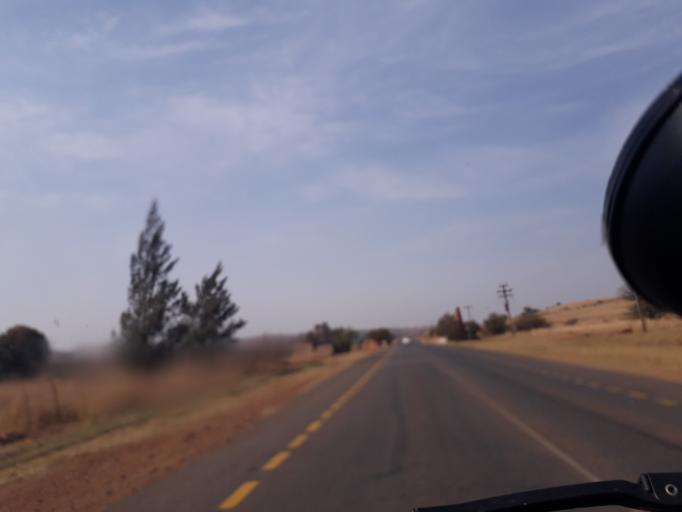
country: ZA
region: Gauteng
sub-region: West Rand District Municipality
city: Krugersdorp
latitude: -26.0226
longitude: 27.7238
